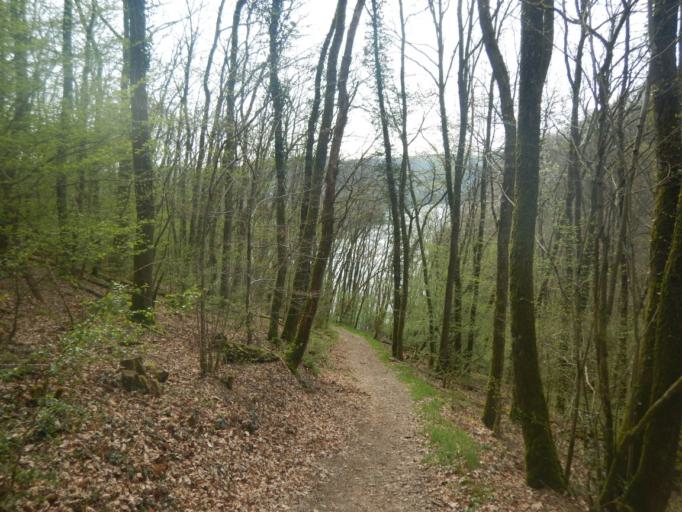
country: LU
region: Diekirch
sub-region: Canton de Wiltz
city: Esch-sur-Sure
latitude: 49.9142
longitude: 5.9176
